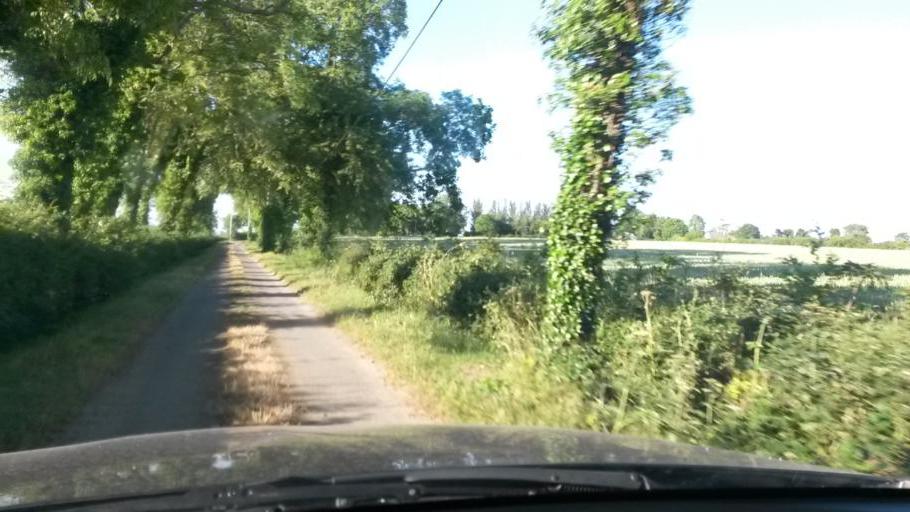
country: IE
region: Leinster
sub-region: Dublin City
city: Finglas
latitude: 53.4425
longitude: -6.3181
